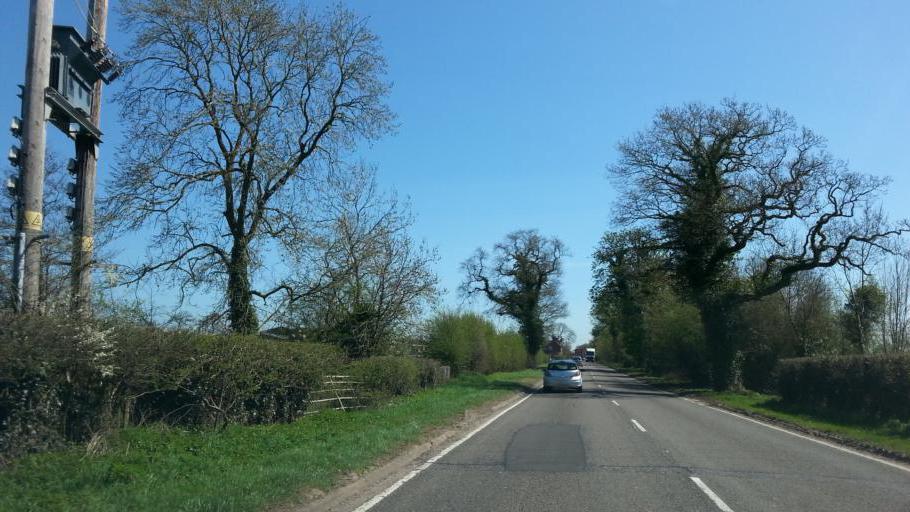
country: GB
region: England
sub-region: Staffordshire
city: Wheaton Aston
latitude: 52.6940
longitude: -2.2207
